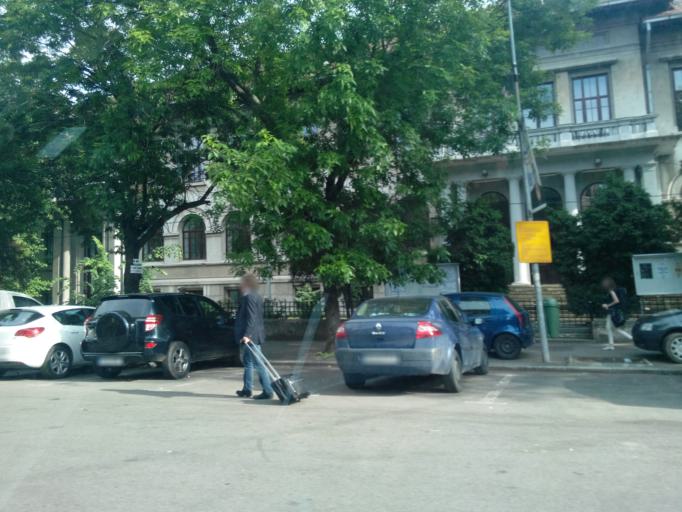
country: RO
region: Bucuresti
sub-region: Municipiul Bucuresti
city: Bucuresti
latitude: 44.4399
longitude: 26.0902
